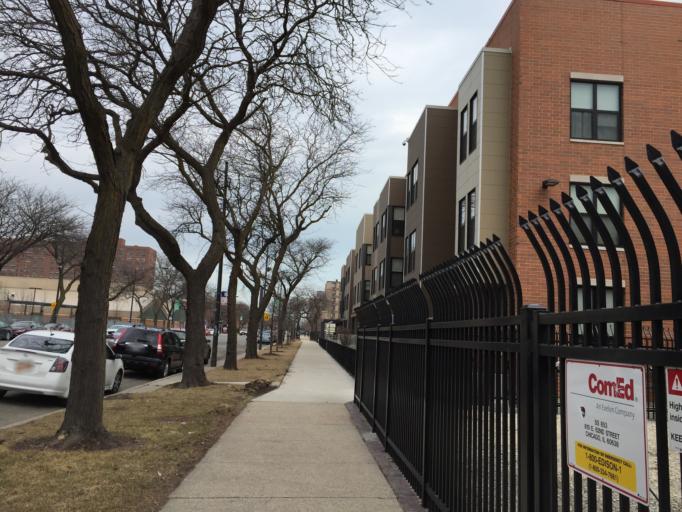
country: US
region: Illinois
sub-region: Cook County
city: Chicago
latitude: 41.7825
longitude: -87.6058
